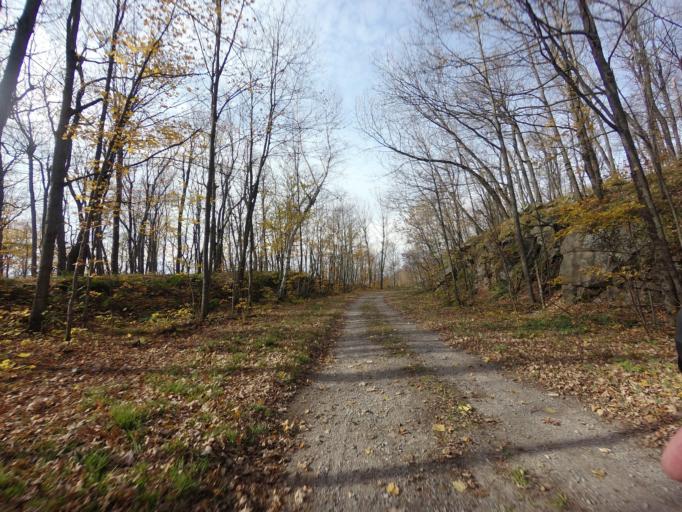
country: CA
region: Quebec
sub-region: Outaouais
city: Wakefield
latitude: 45.5196
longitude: -75.9256
